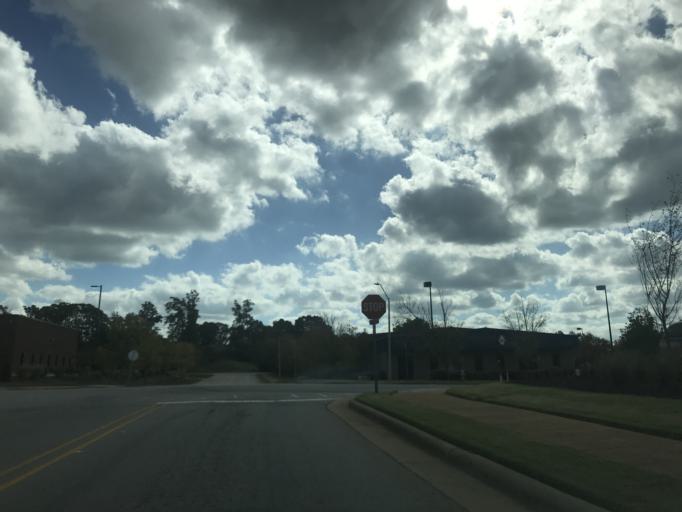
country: US
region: North Carolina
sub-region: Wake County
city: Garner
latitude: 35.7201
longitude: -78.6626
